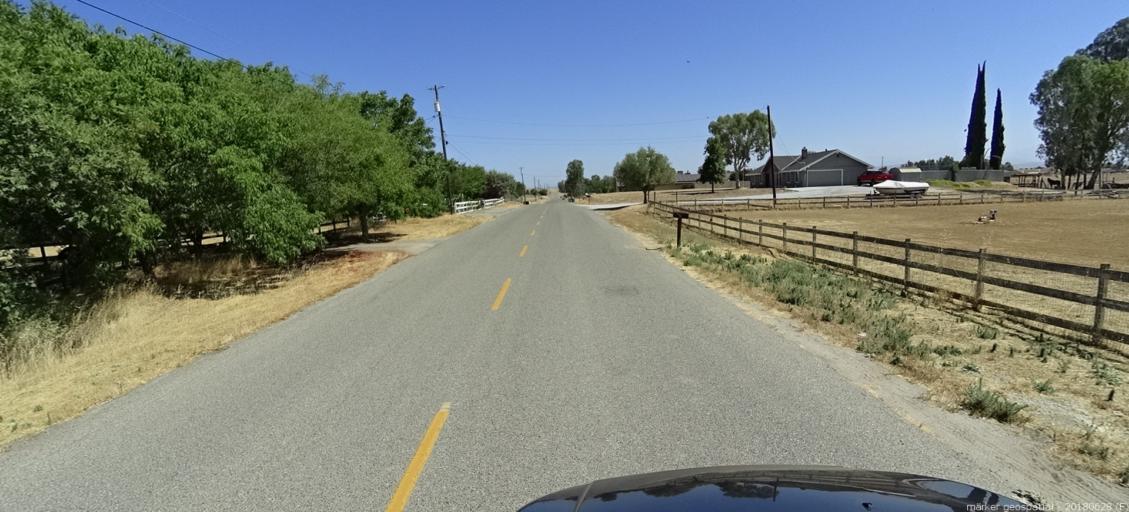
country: US
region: California
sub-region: Madera County
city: Bonadelle Ranchos-Madera Ranchos
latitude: 36.9936
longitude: -119.8685
